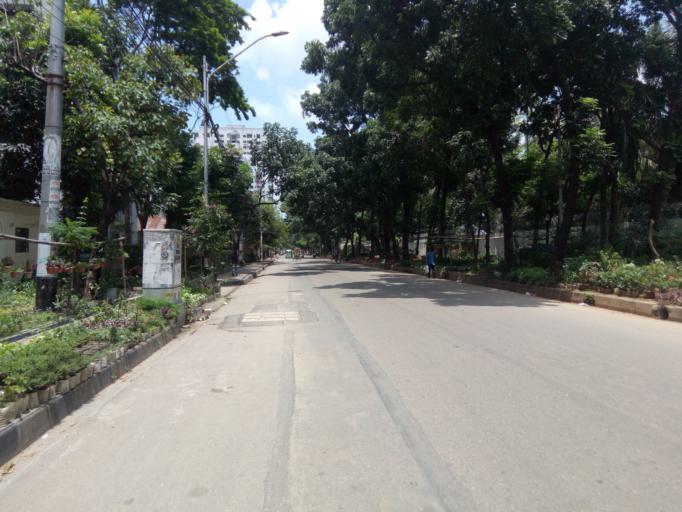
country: BD
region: Dhaka
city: Paltan
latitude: 23.7435
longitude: 90.3987
